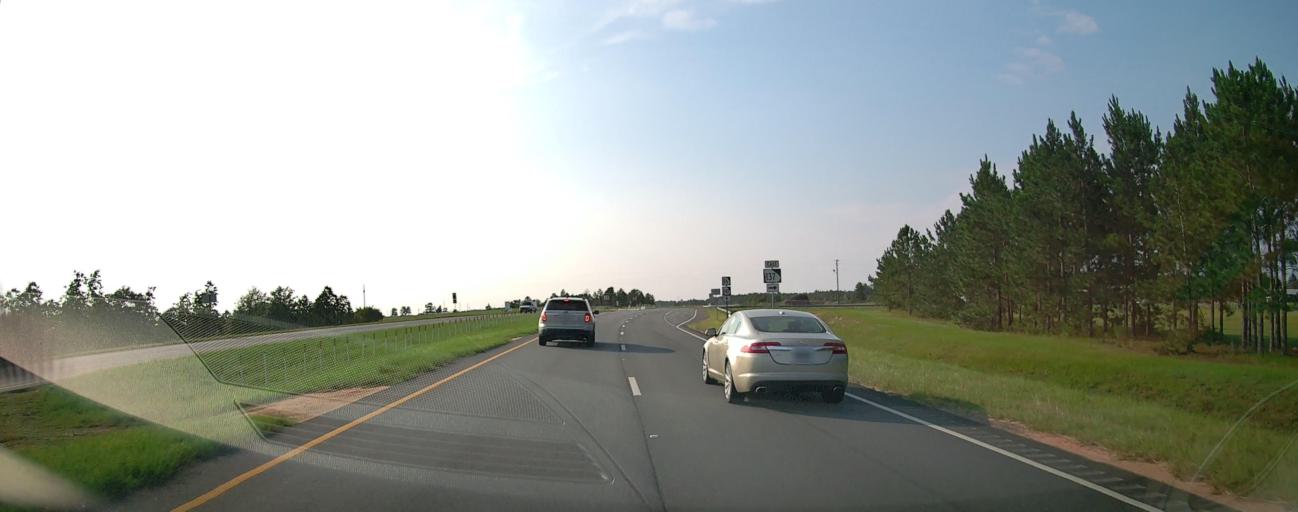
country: US
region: Georgia
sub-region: Taylor County
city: Butler
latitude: 32.5525
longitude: -84.2627
